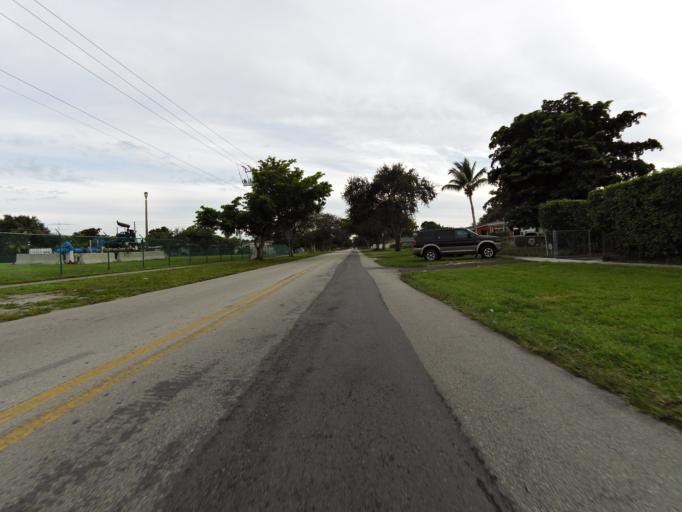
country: US
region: Florida
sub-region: Broward County
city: Pembroke Pines
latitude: 26.0162
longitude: -80.2321
